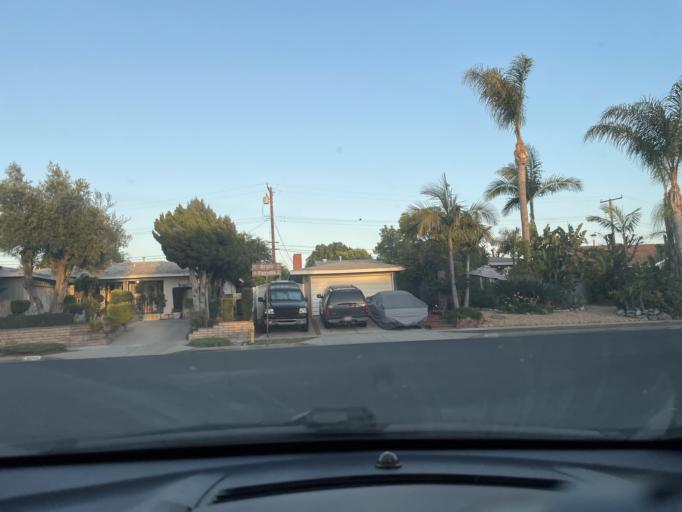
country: US
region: California
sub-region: Los Angeles County
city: La Mirada
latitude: 33.9092
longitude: -118.0241
